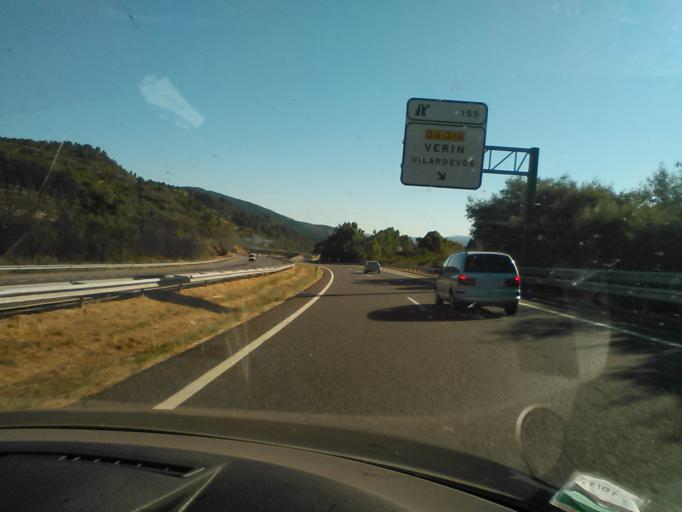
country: ES
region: Galicia
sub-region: Provincia de Ourense
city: Verin
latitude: 41.9423
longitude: -7.3952
